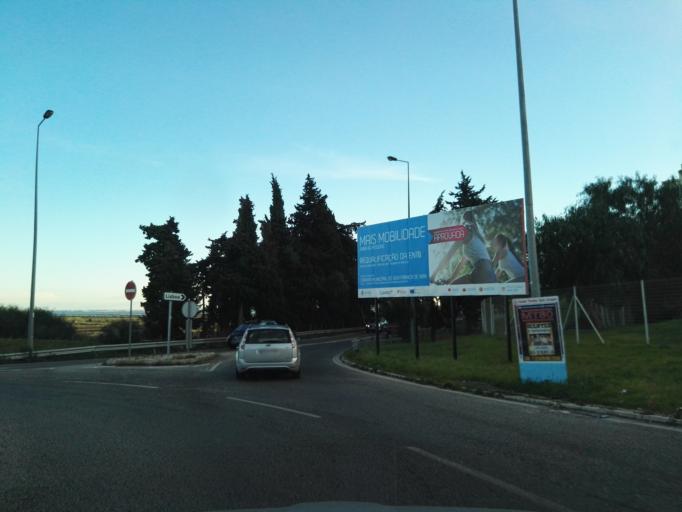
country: PT
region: Lisbon
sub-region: Vila Franca de Xira
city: Vialonga
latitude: 38.8764
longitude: -9.0527
